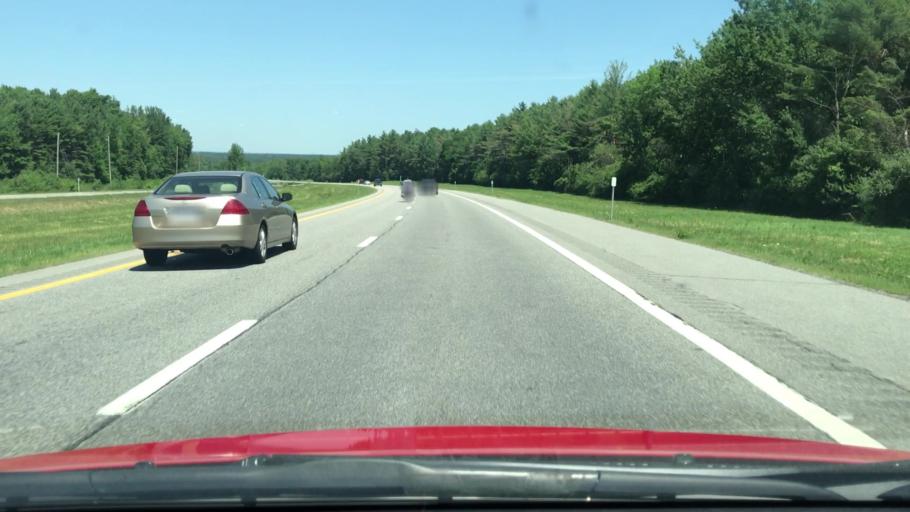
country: US
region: New York
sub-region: Essex County
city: Keeseville
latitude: 44.4587
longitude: -73.4856
